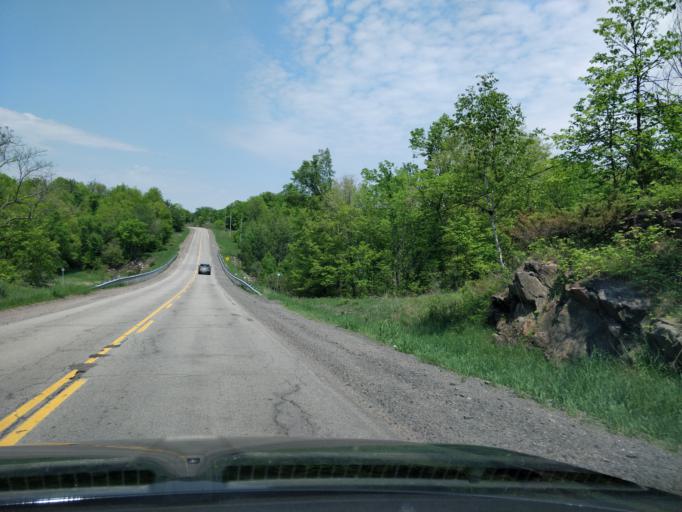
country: CA
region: Ontario
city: Perth
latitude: 44.7391
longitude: -76.3917
